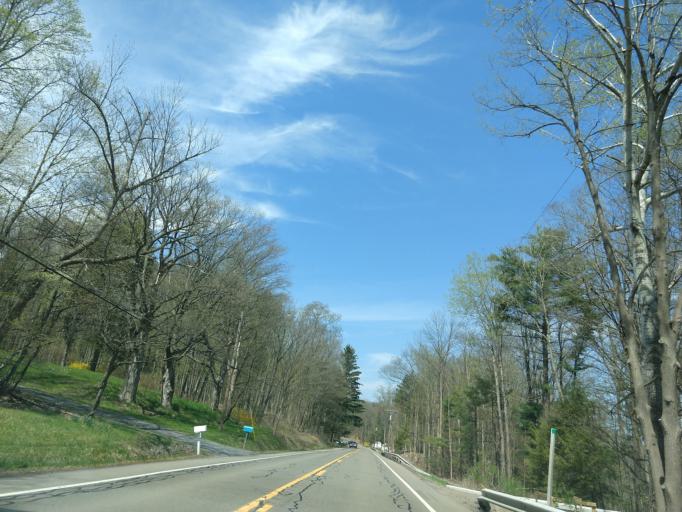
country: US
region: New York
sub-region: Tompkins County
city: Trumansburg
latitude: 42.5375
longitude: -76.5879
